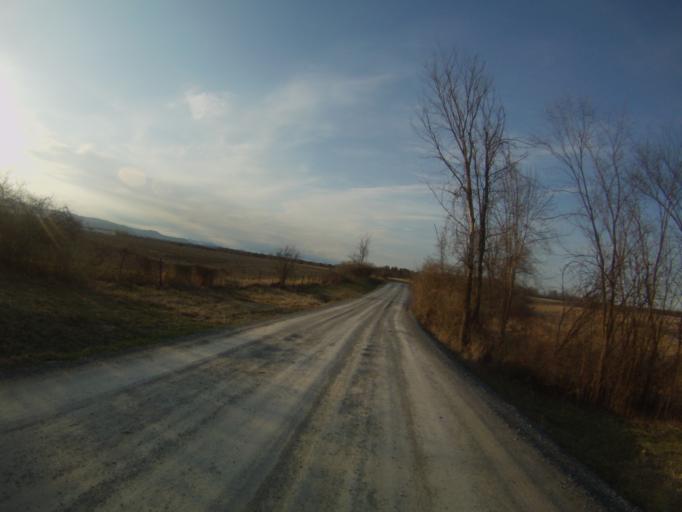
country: US
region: New York
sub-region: Essex County
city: Port Henry
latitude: 44.0795
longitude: -73.3510
